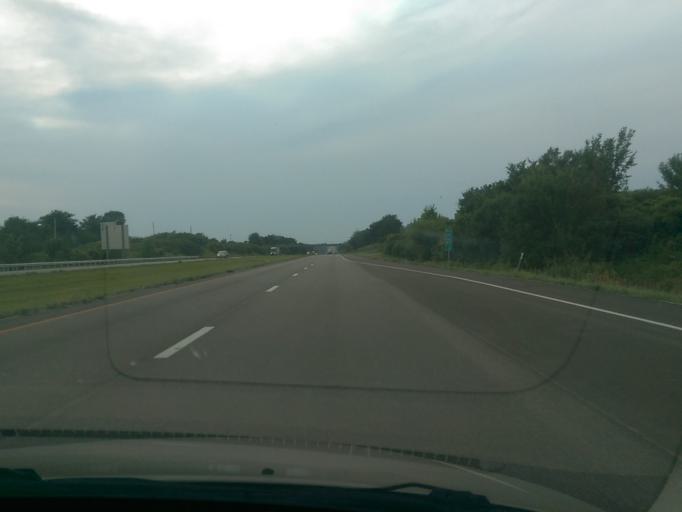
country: US
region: Missouri
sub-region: Andrew County
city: Savannah
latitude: 39.8910
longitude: -94.8637
